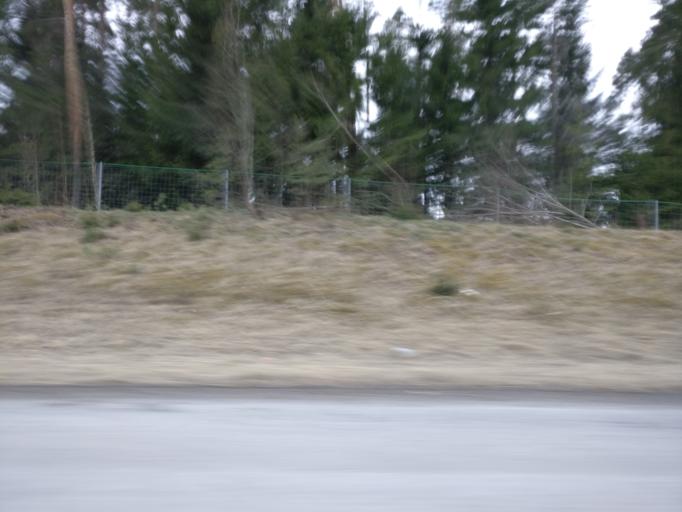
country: FI
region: Haeme
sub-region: Haemeenlinna
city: Parola
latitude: 61.0637
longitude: 24.3253
